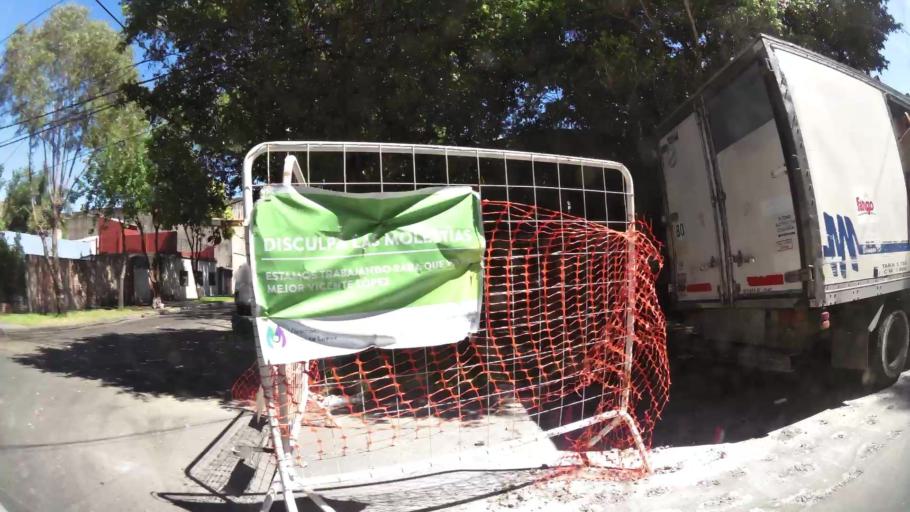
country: AR
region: Buenos Aires
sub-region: Partido de General San Martin
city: General San Martin
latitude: -34.5383
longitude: -58.5426
